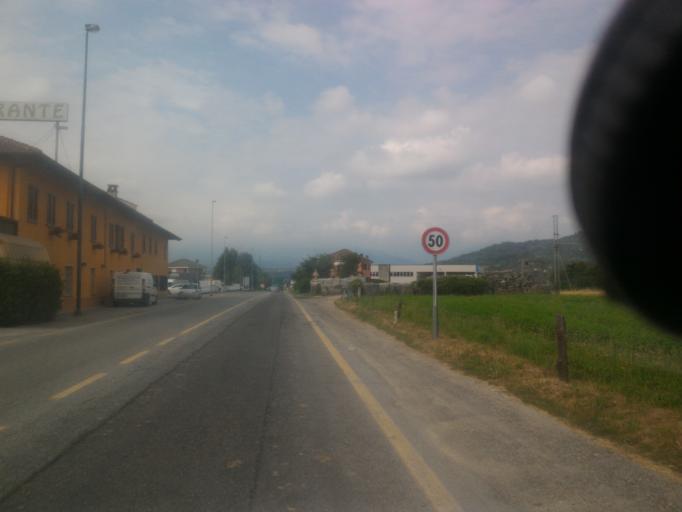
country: IT
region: Piedmont
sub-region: Provincia di Torino
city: Osasco
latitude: 44.8508
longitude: 7.3185
